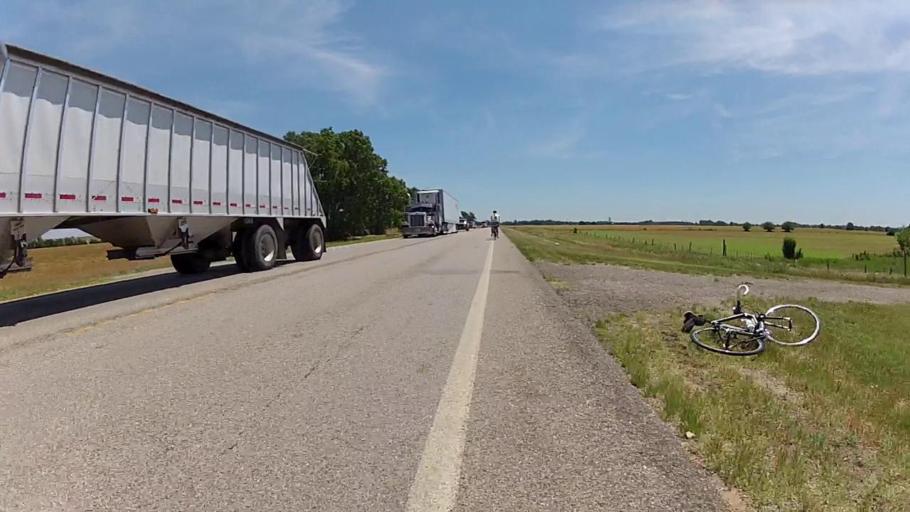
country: US
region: Kansas
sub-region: Barber County
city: Medicine Lodge
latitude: 37.2534
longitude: -98.4518
